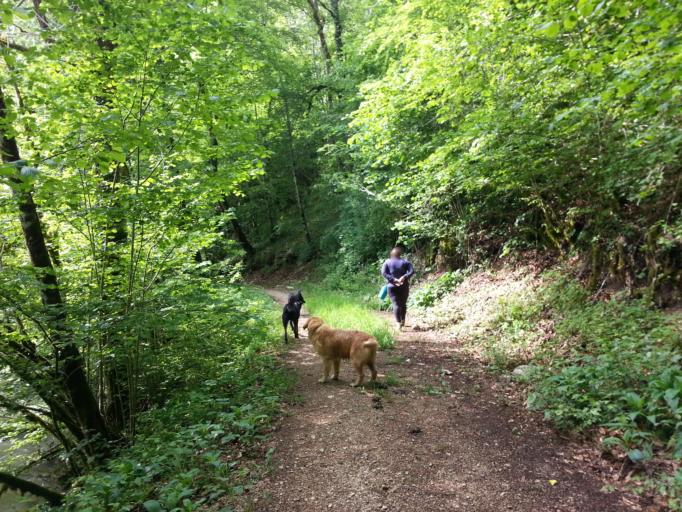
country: FR
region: Franche-Comte
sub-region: Departement du Doubs
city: Levier
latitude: 47.0024
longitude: 6.0007
